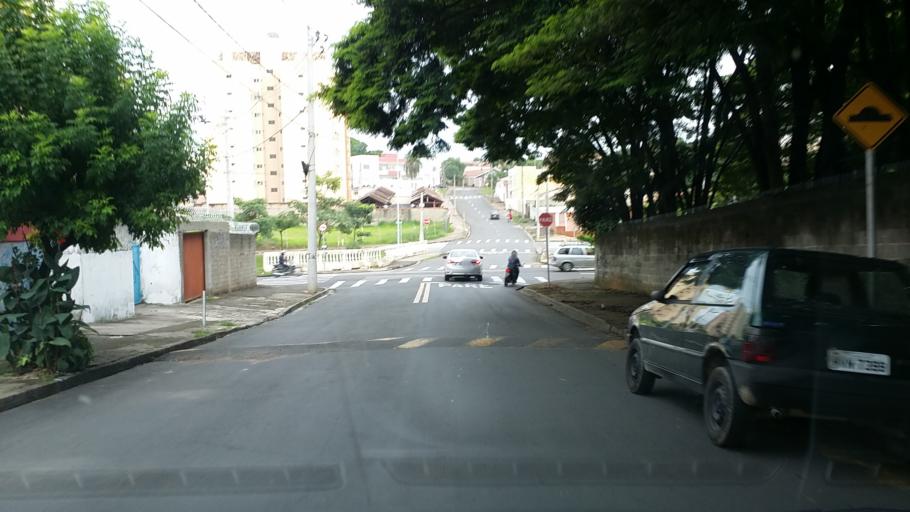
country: BR
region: Sao Paulo
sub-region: Indaiatuba
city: Indaiatuba
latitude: -23.0961
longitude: -47.2190
